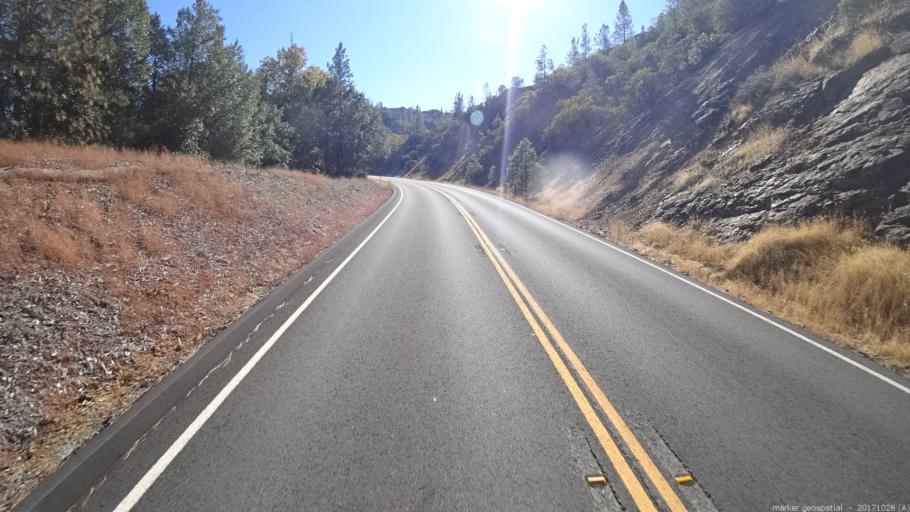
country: US
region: California
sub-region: Shasta County
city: Shasta
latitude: 40.6116
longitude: -122.5657
